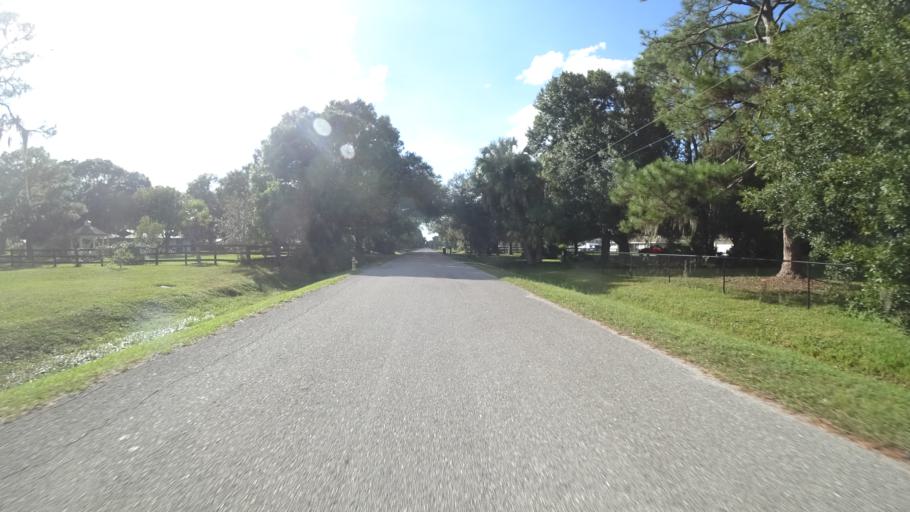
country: US
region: Florida
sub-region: Manatee County
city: Ellenton
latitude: 27.4874
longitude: -82.4769
